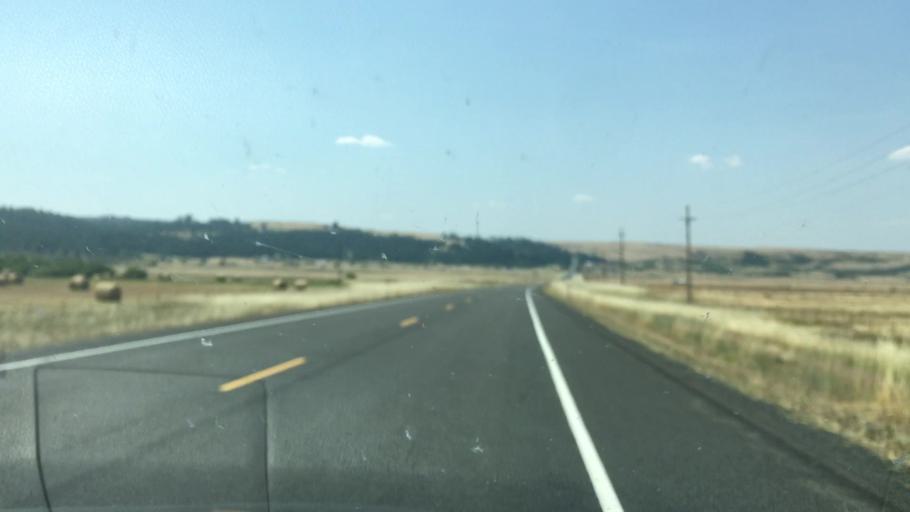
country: US
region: Idaho
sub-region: Idaho County
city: Grangeville
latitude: 45.8913
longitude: -116.1951
